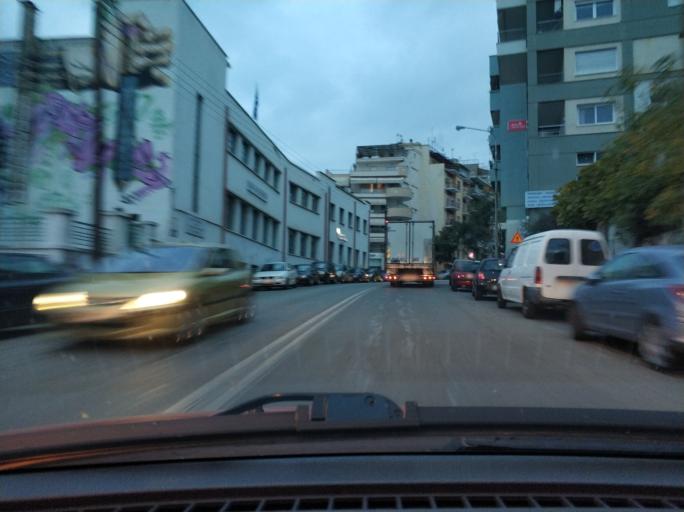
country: GR
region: East Macedonia and Thrace
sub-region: Nomos Kavalas
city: Kavala
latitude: 40.9355
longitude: 24.4004
